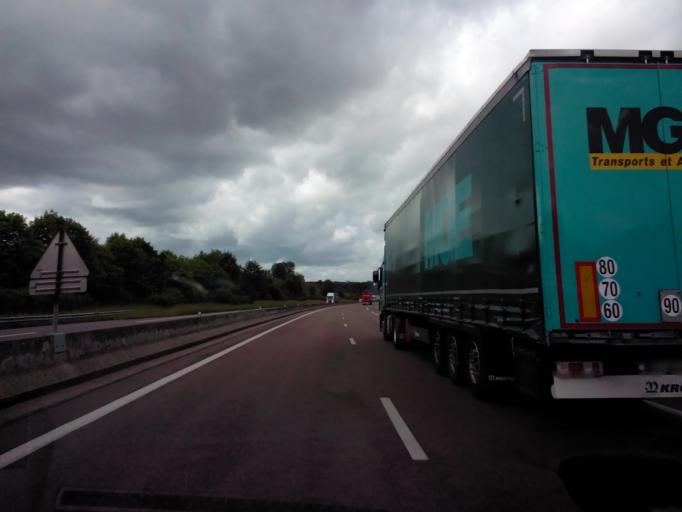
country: FR
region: Lorraine
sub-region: Departement des Vosges
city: Chatenois
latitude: 48.4078
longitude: 5.8715
